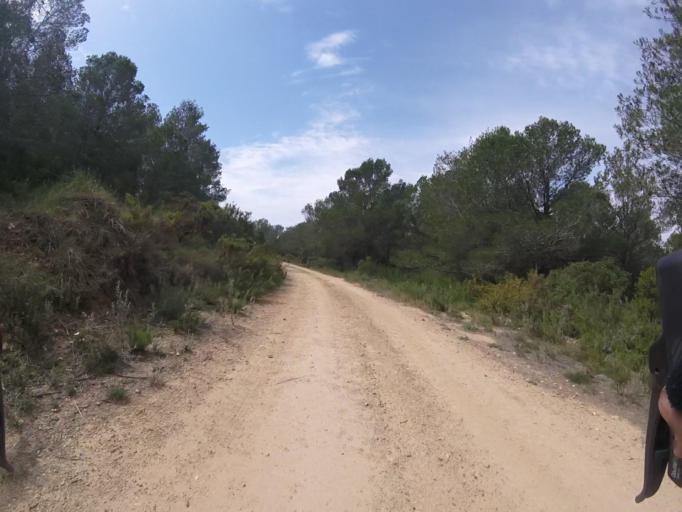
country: ES
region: Valencia
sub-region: Provincia de Castello
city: Cuevas de Vinroma
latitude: 40.2694
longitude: 0.1144
